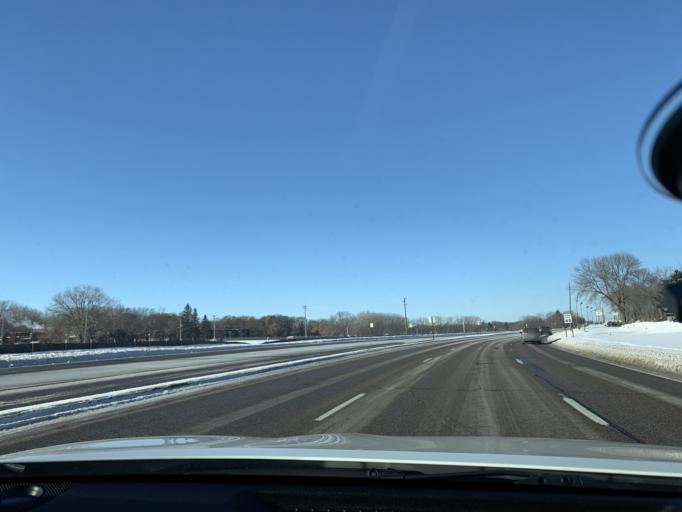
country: US
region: Minnesota
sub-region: Anoka County
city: Coon Rapids
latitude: 45.1517
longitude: -93.3000
